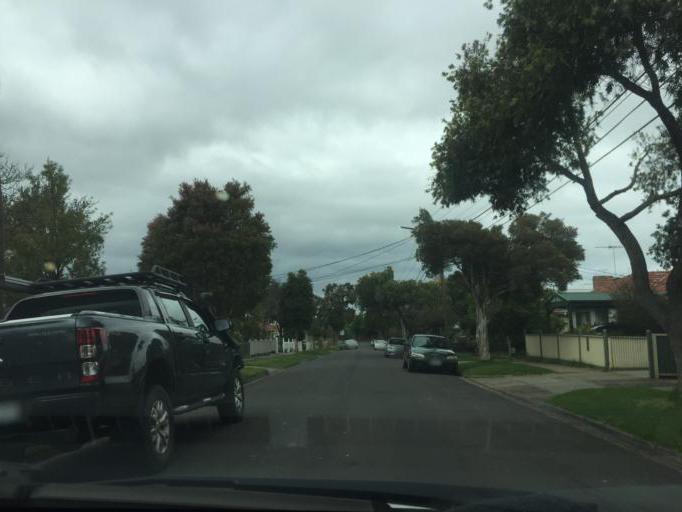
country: AU
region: Victoria
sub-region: Maribyrnong
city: Kingsville
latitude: -37.8175
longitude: 144.8730
